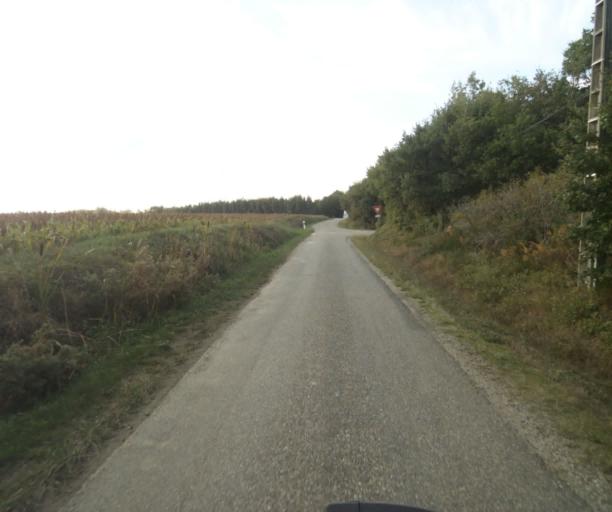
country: FR
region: Midi-Pyrenees
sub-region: Departement de la Haute-Garonne
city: Launac
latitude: 43.8138
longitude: 1.0969
